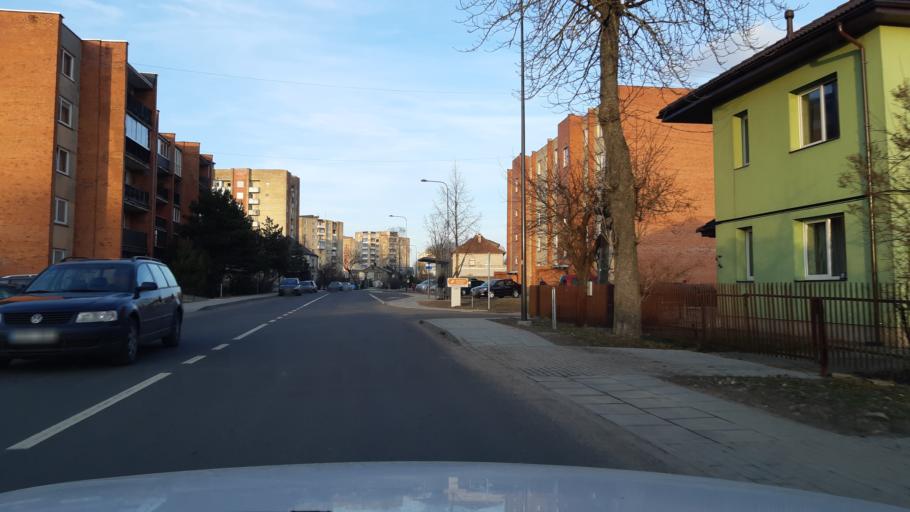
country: LT
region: Kauno apskritis
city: Dainava (Kaunas)
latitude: 54.8891
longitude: 23.9433
